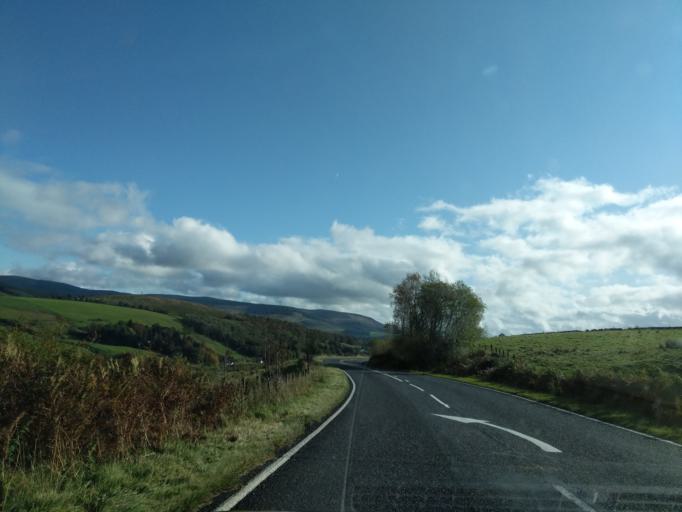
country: GB
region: Scotland
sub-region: Dumfries and Galloway
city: Moffat
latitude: 55.3530
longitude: -3.4670
